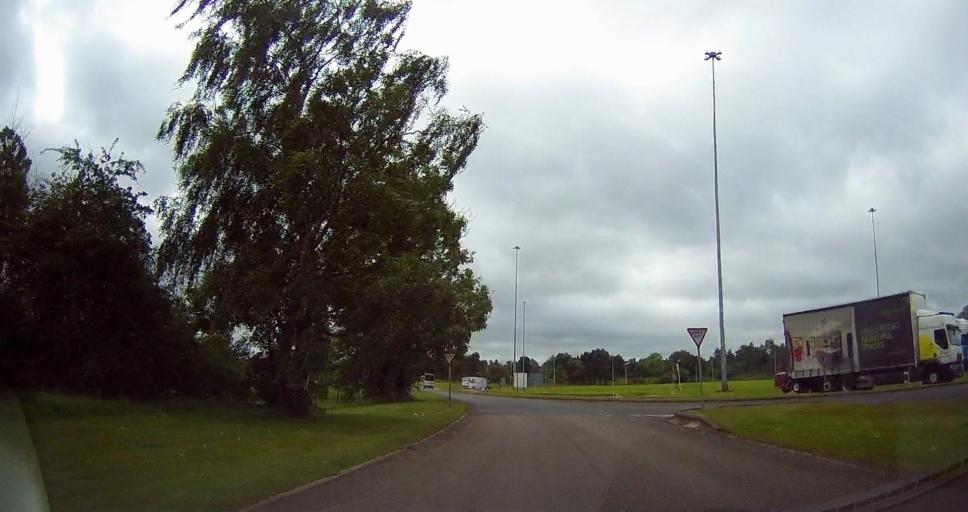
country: GB
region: Scotland
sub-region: South Lanarkshire
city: Bothwell
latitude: 55.8146
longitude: -4.0603
